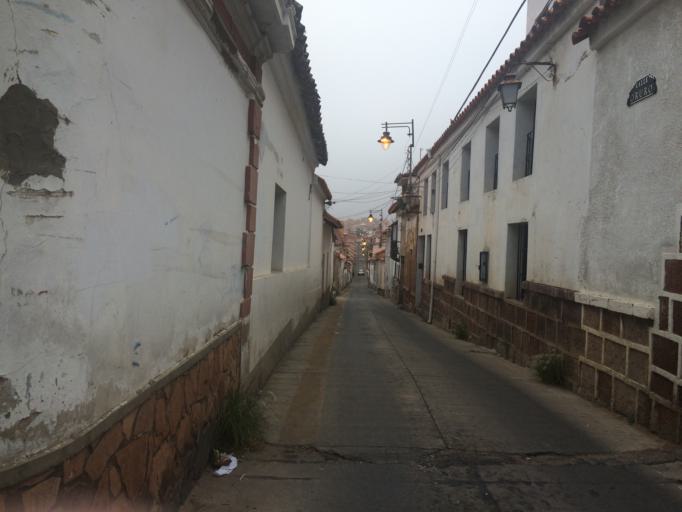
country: BO
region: Chuquisaca
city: Sucre
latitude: -19.0530
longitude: -65.2560
